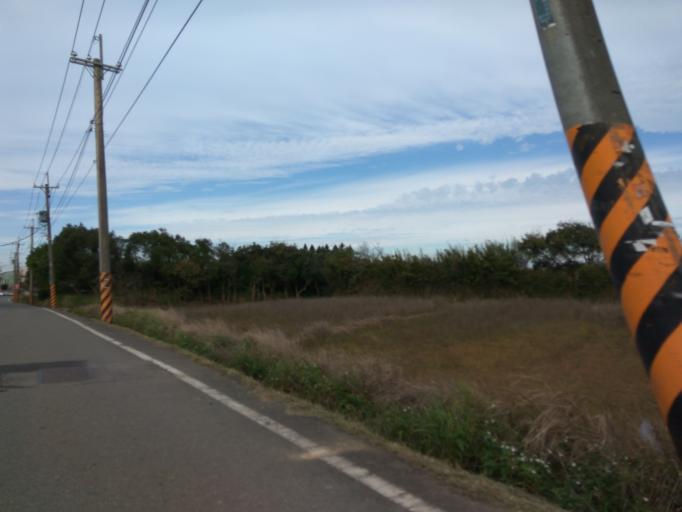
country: TW
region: Taiwan
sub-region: Hsinchu
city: Zhubei
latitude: 24.9600
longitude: 121.1029
